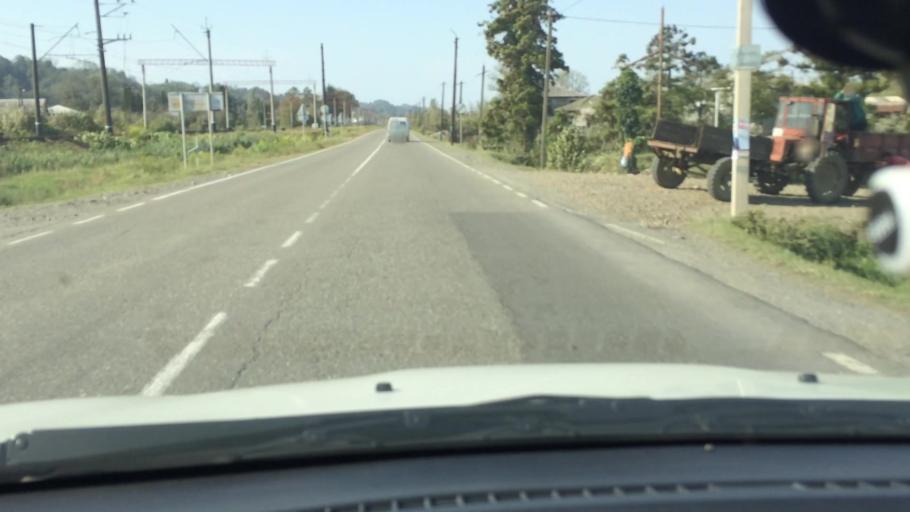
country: GE
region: Guria
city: Lanchkhuti
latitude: 42.0776
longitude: 41.9134
